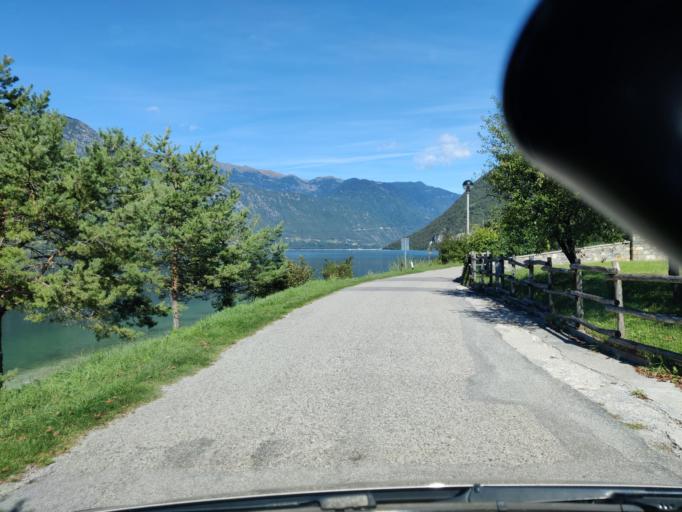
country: IT
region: Lombardy
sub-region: Provincia di Brescia
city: Anfo
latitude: 45.7680
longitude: 10.5180
